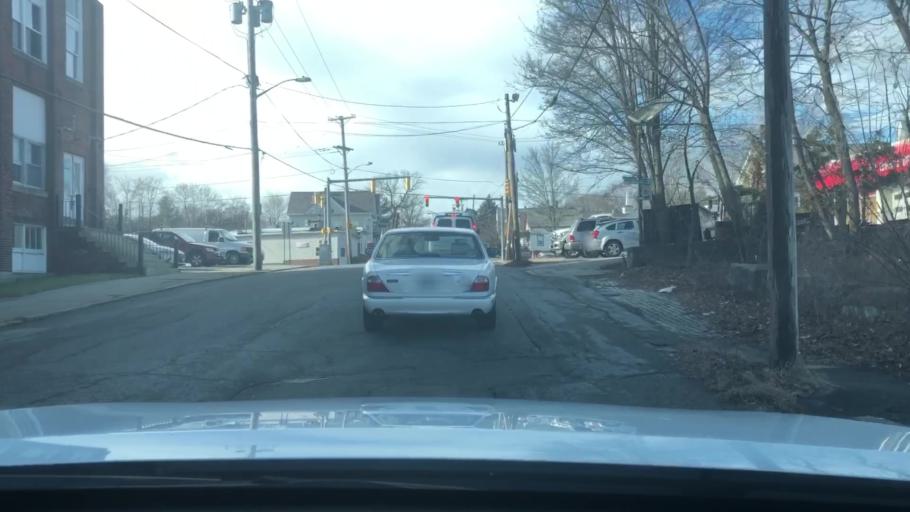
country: US
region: Rhode Island
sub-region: Providence County
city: Woonsocket
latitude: 42.0140
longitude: -71.5130
